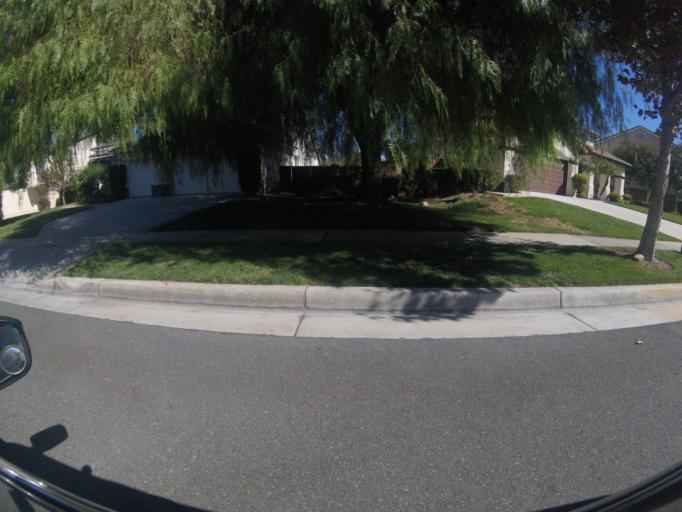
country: US
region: California
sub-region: San Bernardino County
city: Mentone
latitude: 34.0745
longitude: -117.1469
